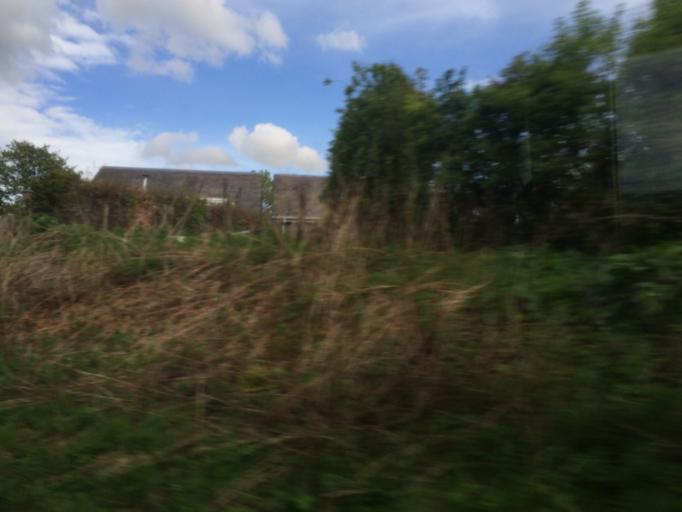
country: GB
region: Scotland
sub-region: Clackmannanshire
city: Menstrie
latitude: 56.2473
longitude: -3.8828
